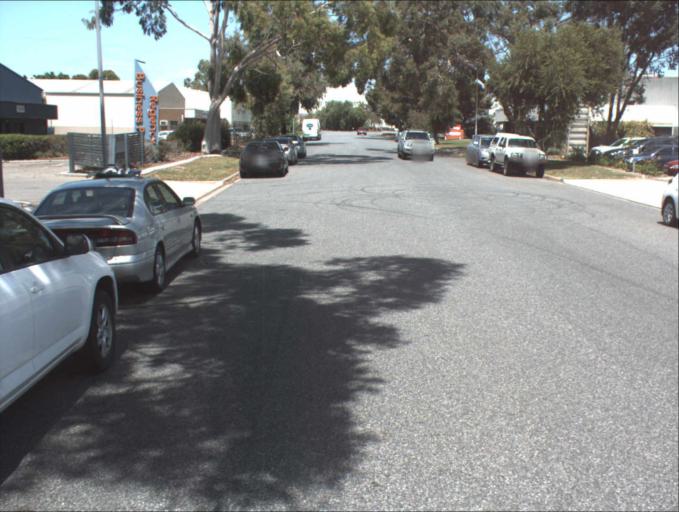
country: AU
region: South Australia
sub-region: Port Adelaide Enfield
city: Blair Athol
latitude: -34.8515
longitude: 138.5673
